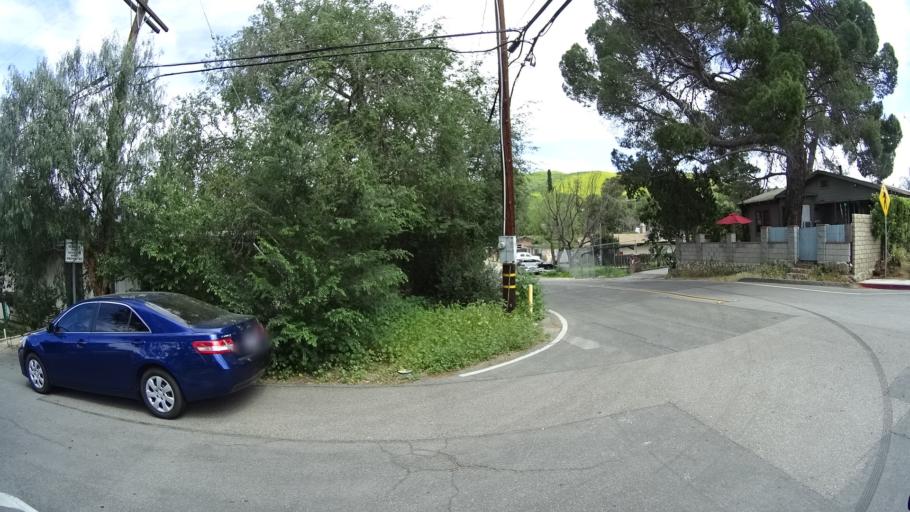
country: US
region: California
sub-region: Ventura County
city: Thousand Oaks
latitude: 34.1743
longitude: -118.8409
